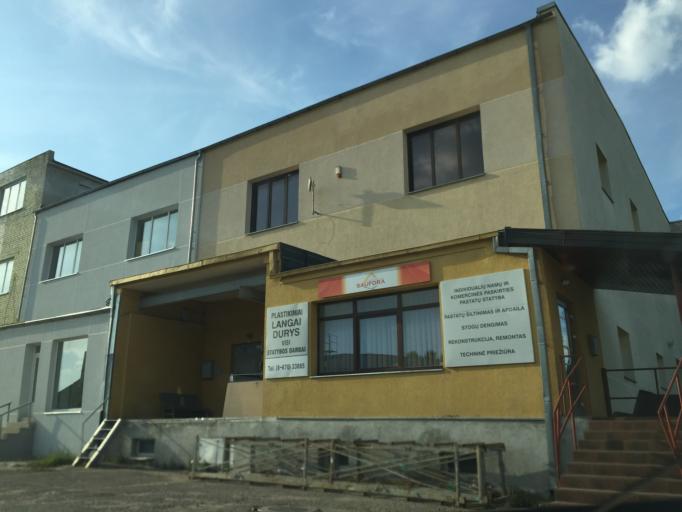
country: LT
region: Panevezys
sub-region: Panevezys City
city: Panevezys
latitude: 55.7450
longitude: 24.3750
